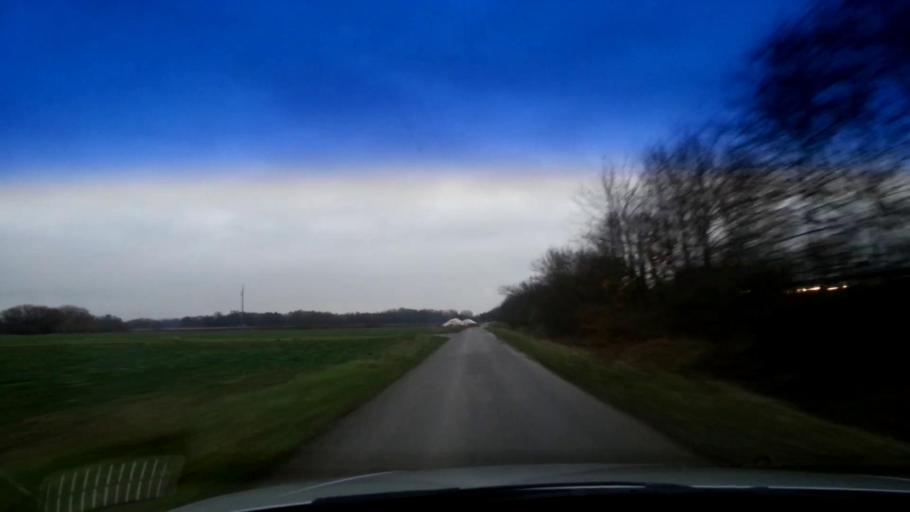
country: DE
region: Bavaria
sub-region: Upper Franconia
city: Bischberg
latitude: 49.9221
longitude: 10.8288
